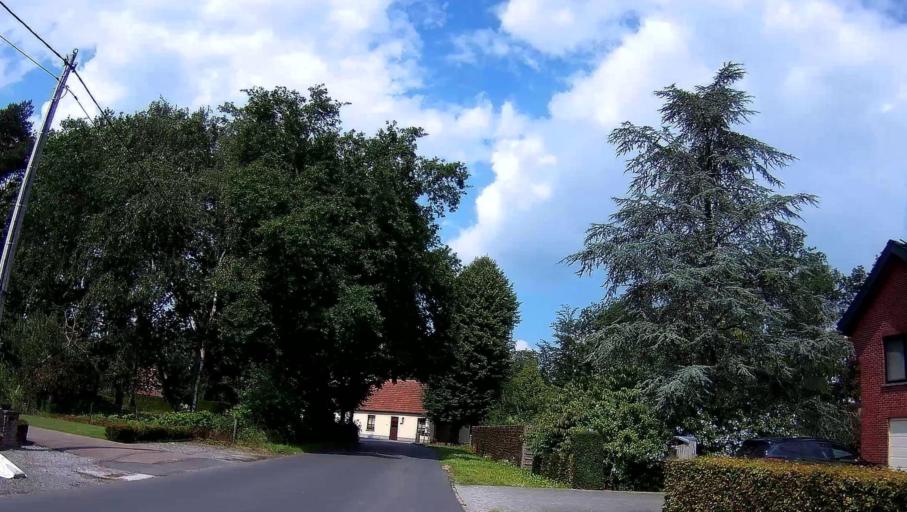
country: BE
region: Flanders
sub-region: Provincie Limburg
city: Leopoldsburg
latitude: 51.1864
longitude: 5.2539
